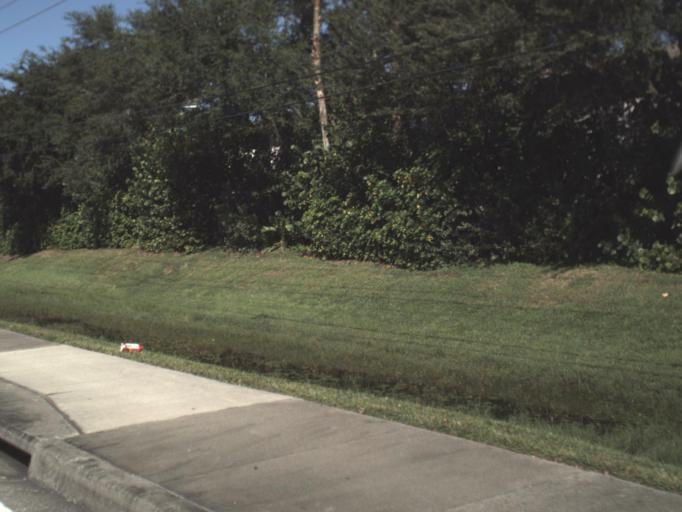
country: US
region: Florida
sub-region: Collier County
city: Pine Ridge
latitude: 26.2118
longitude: -81.7559
